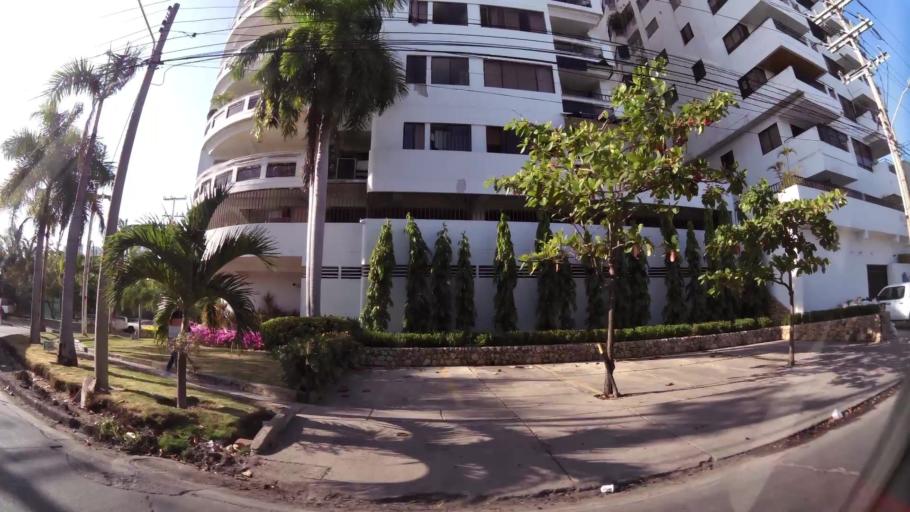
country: CO
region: Bolivar
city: Cartagena
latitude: 10.3959
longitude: -75.5579
